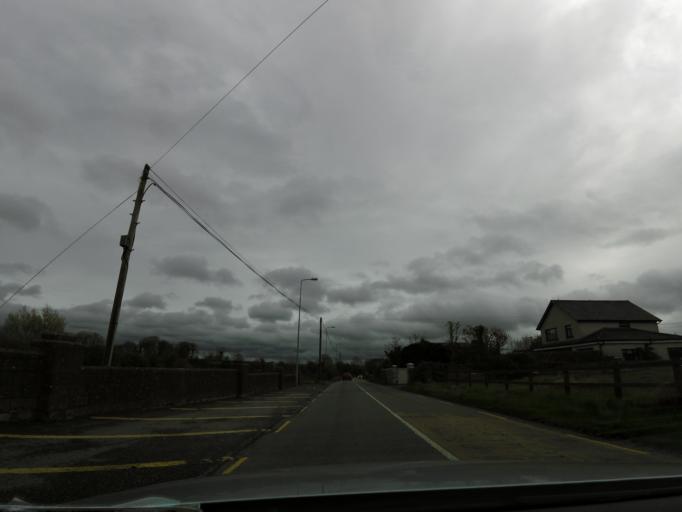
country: IE
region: Leinster
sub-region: Kilkenny
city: Ballyragget
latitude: 52.7323
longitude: -7.3926
